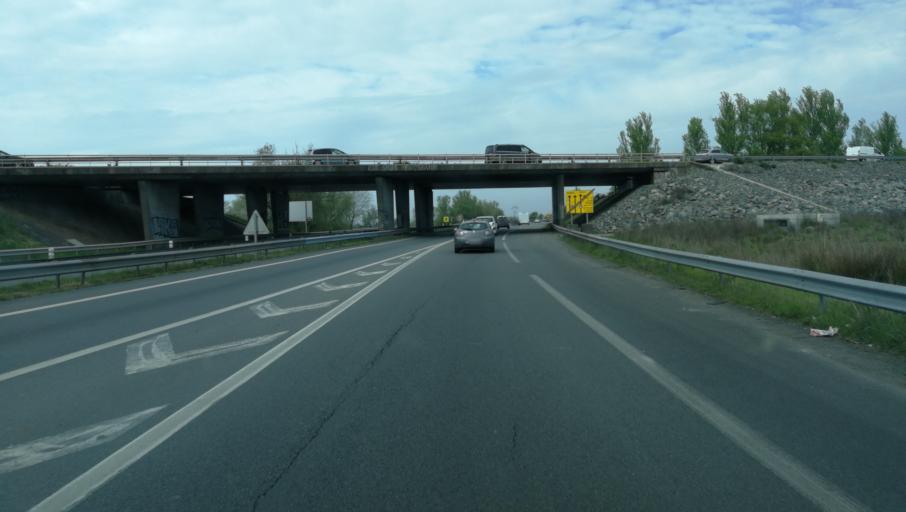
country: FR
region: Pays de la Loire
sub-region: Departement de la Loire-Atlantique
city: Trignac
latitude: 47.3054
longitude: -2.2053
